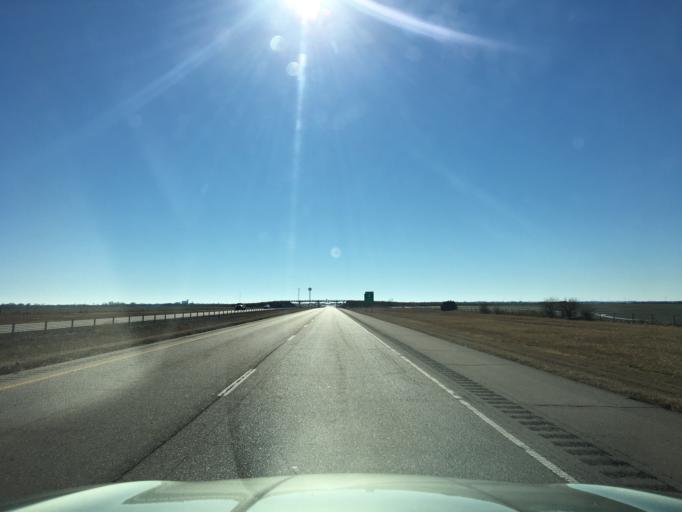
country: US
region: Oklahoma
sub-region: Kay County
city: Blackwell
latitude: 36.9609
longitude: -97.3458
